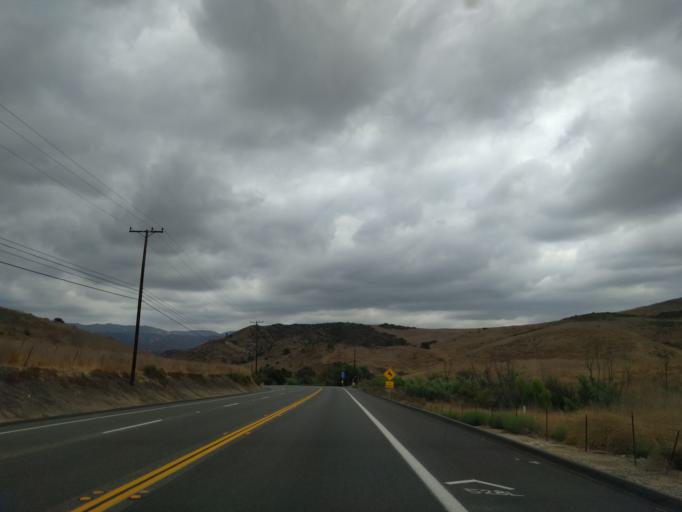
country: US
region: California
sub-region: Orange County
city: North Tustin
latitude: 33.7682
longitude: -117.7320
